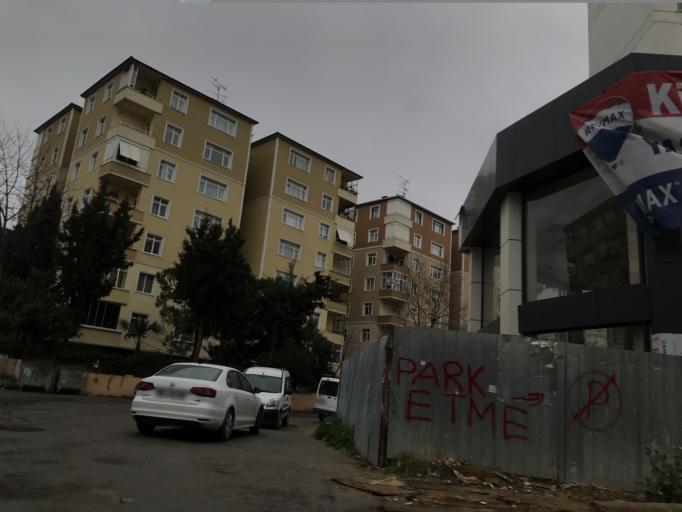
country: TR
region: Istanbul
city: Pendik
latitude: 40.8842
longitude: 29.2277
